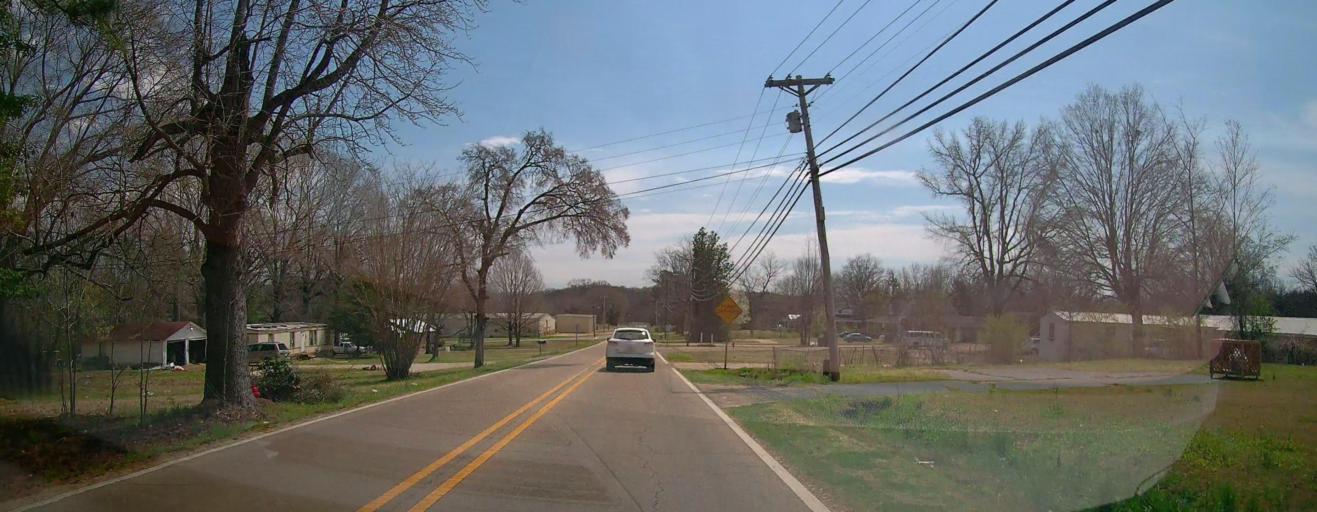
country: US
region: Mississippi
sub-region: Union County
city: New Albany
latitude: 34.4752
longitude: -88.9953
